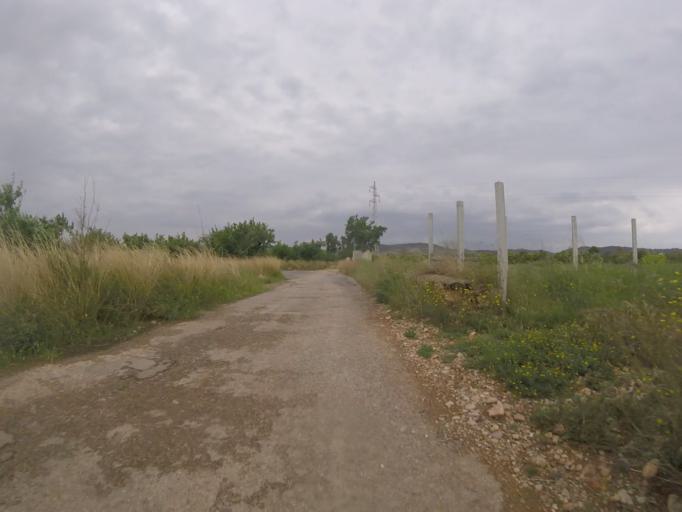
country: ES
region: Valencia
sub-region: Provincia de Castello
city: Torreblanca
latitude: 40.2210
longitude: 0.2124
